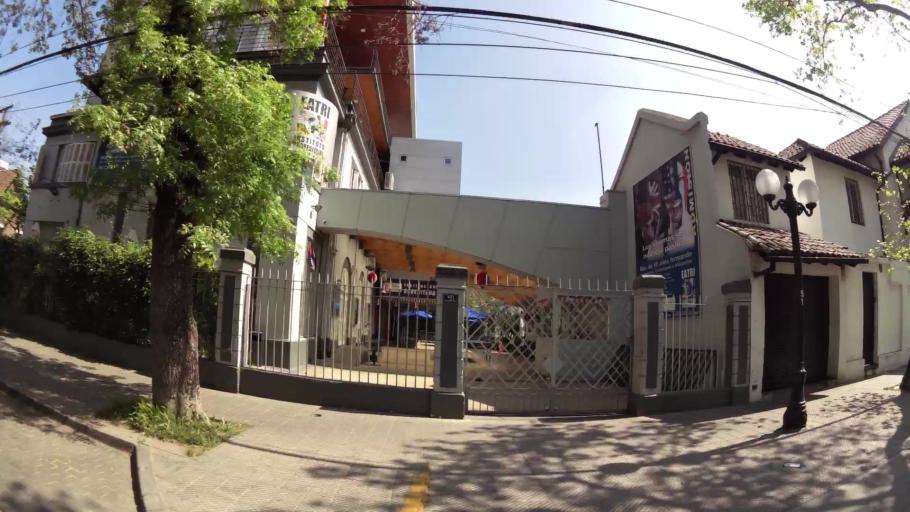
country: CL
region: Santiago Metropolitan
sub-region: Provincia de Santiago
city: Santiago
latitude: -33.4392
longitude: -70.6276
